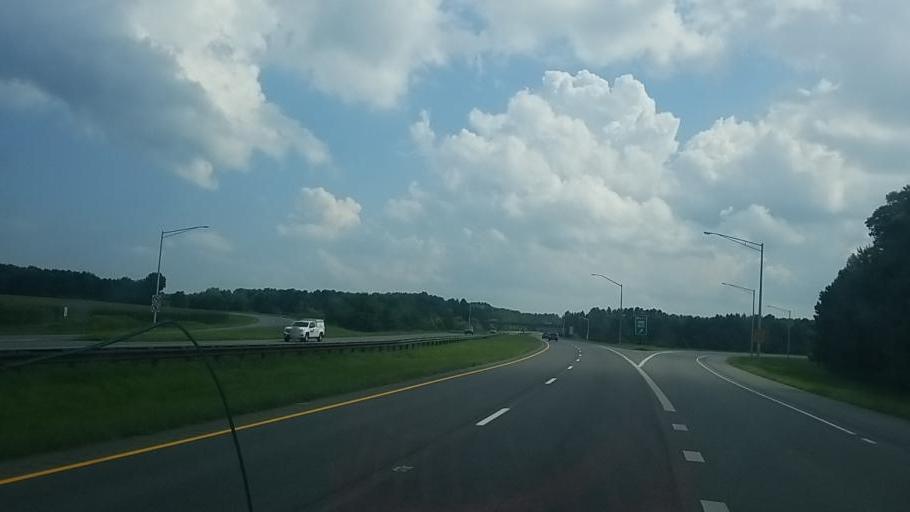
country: US
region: Maryland
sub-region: Worcester County
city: Ocean Pines
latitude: 38.3813
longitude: -75.2067
